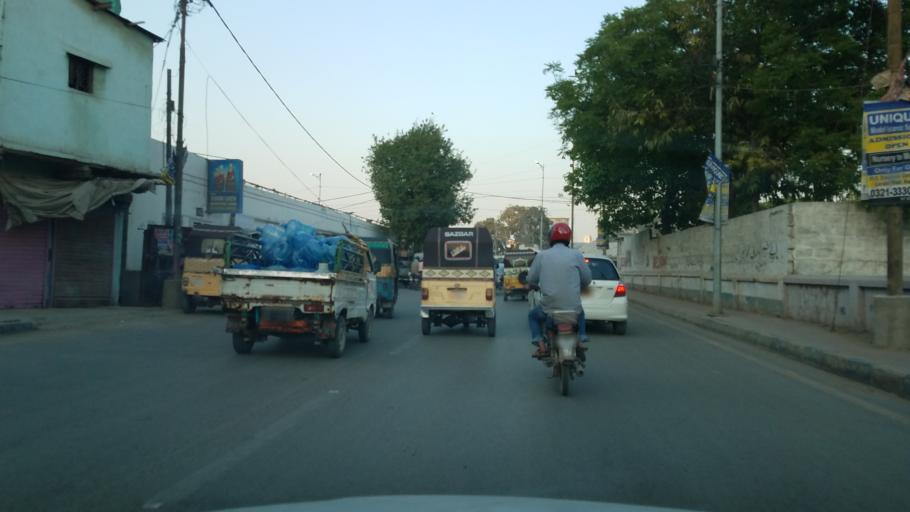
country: PK
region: Sindh
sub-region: Karachi District
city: Karachi
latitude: 24.8811
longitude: 67.0224
